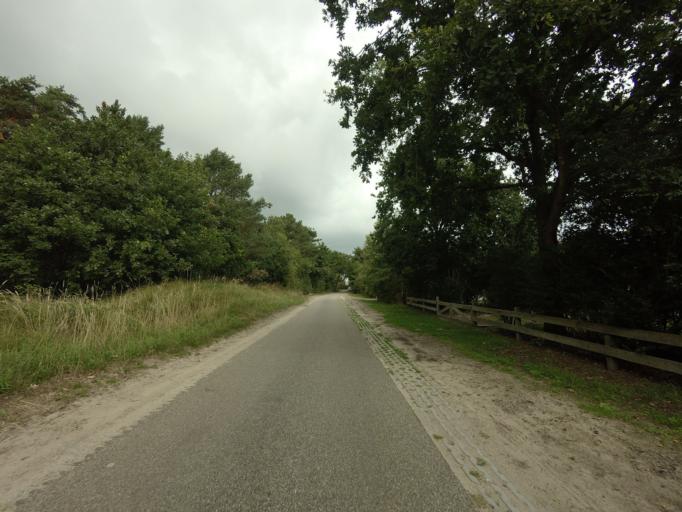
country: NL
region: Friesland
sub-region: Gemeente Ameland
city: Hollum
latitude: 53.4469
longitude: 5.6269
